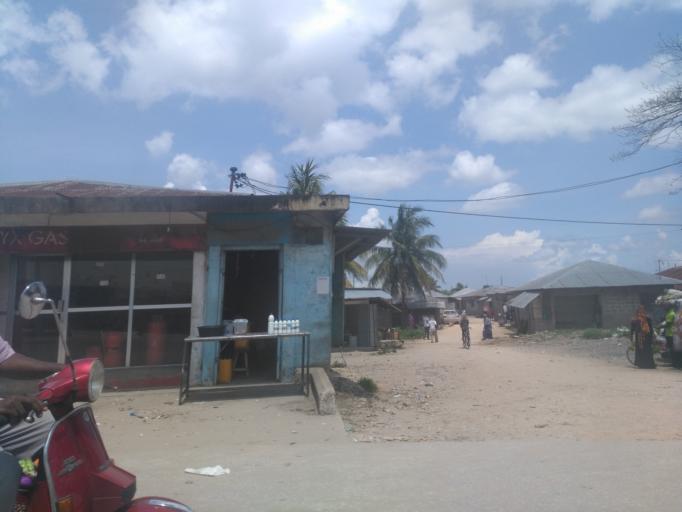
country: TZ
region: Zanzibar Urban/West
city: Zanzibar
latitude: -6.1632
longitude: 39.2173
